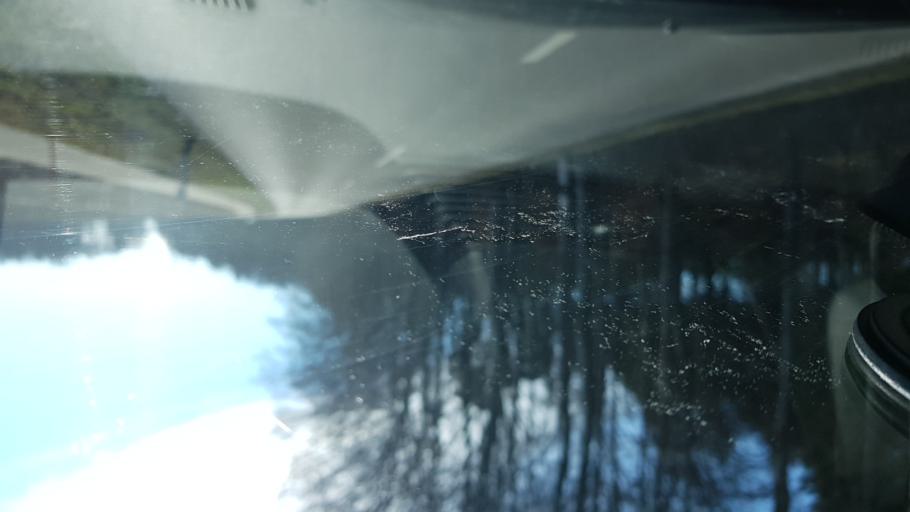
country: DE
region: Bavaria
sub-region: Upper Bavaria
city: Oberschweinbach
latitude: 48.2253
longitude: 11.1735
